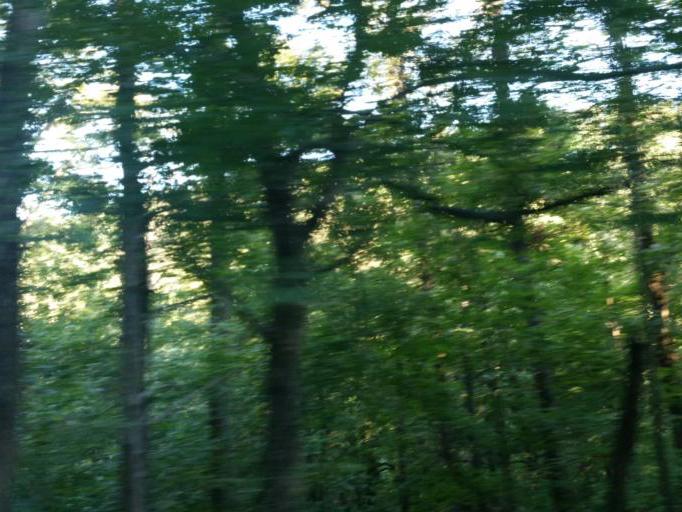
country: US
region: Tennessee
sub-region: Knox County
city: Knoxville
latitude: 35.9253
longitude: -83.9483
